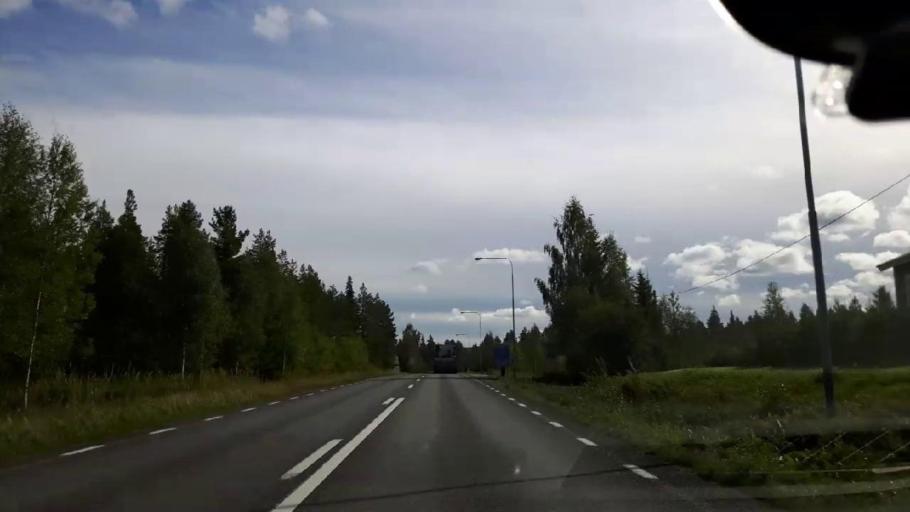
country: SE
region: Jaemtland
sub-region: Braecke Kommun
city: Braecke
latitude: 63.1756
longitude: 15.5330
